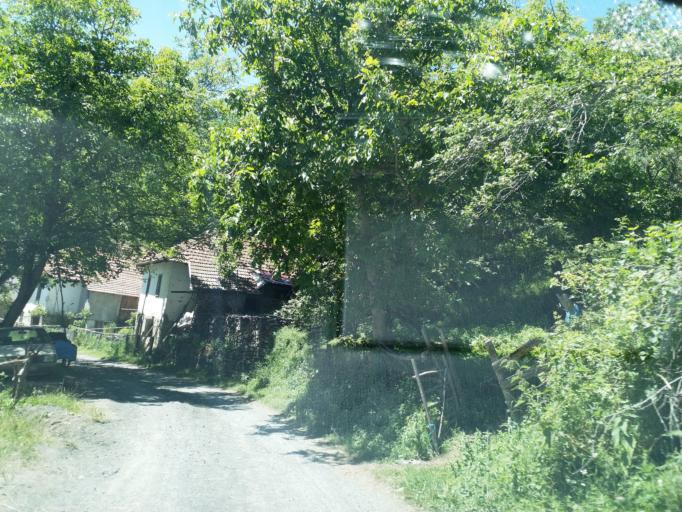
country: XK
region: Mitrovica
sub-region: Komuna e Leposaviqit
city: Leposaviq
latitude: 43.2720
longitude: 20.8739
